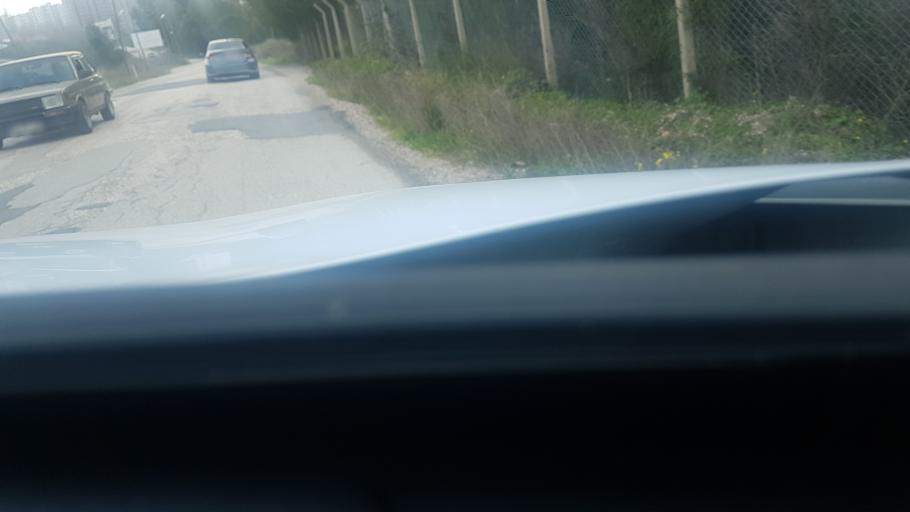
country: TR
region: Adana
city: Seyhan
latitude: 37.0578
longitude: 35.2549
